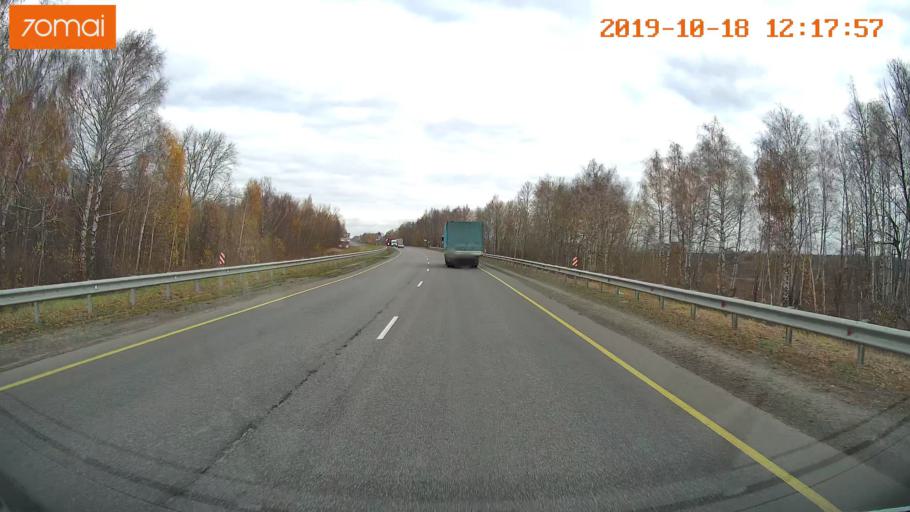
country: RU
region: Rjazan
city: Zakharovo
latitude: 54.4618
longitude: 39.4517
